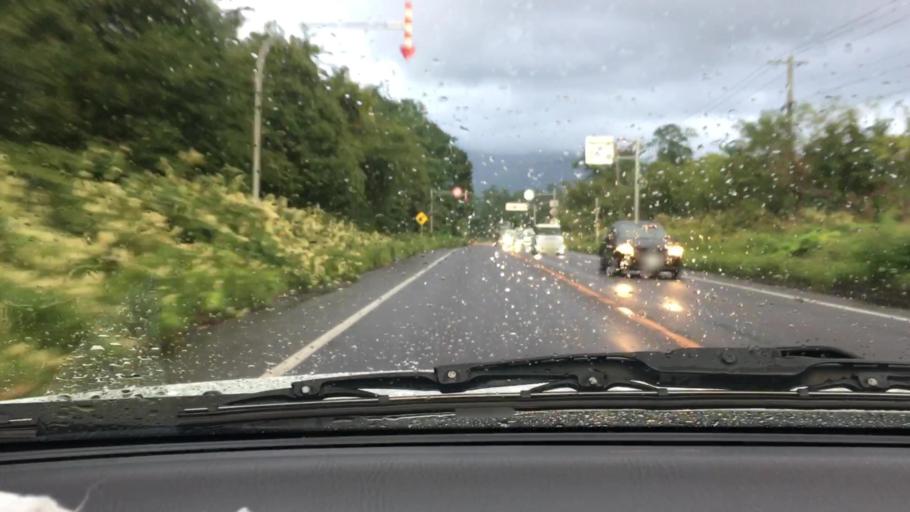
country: JP
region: Hokkaido
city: Nanae
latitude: 42.0808
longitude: 140.5920
